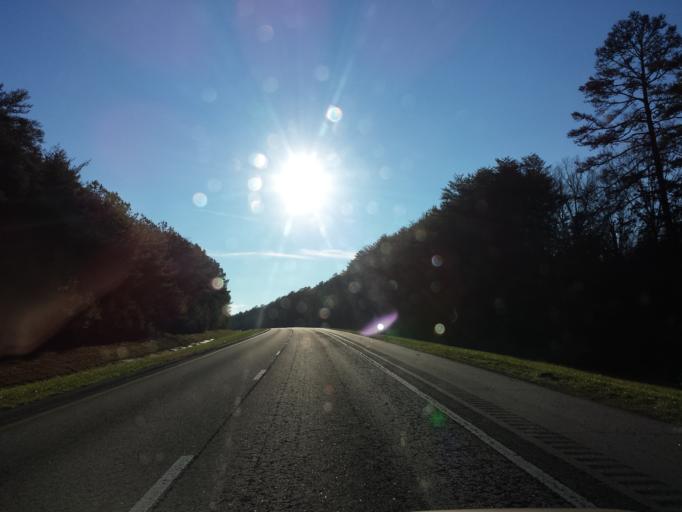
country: US
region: Alabama
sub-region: Hale County
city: Moundville
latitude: 33.0493
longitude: -87.7235
